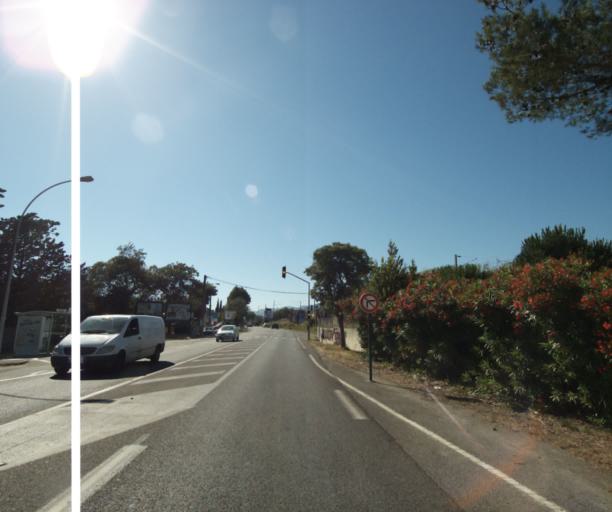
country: FR
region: Provence-Alpes-Cote d'Azur
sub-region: Departement du Var
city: La Garde
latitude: 43.1136
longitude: 5.9898
